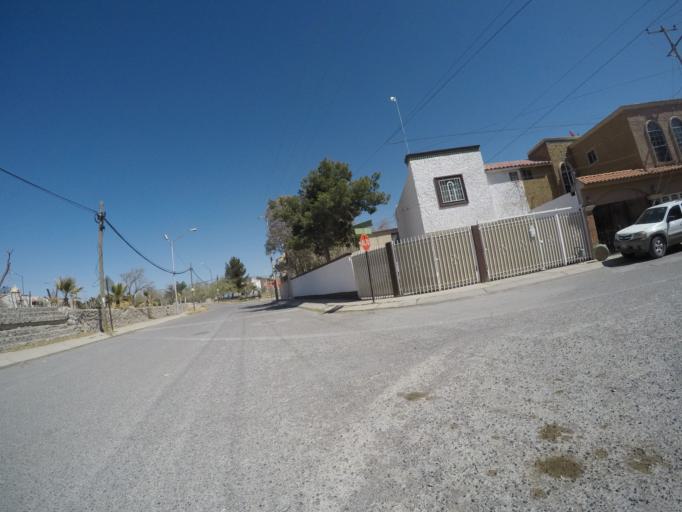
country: MX
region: Chihuahua
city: Ciudad Juarez
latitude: 31.6906
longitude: -106.4174
